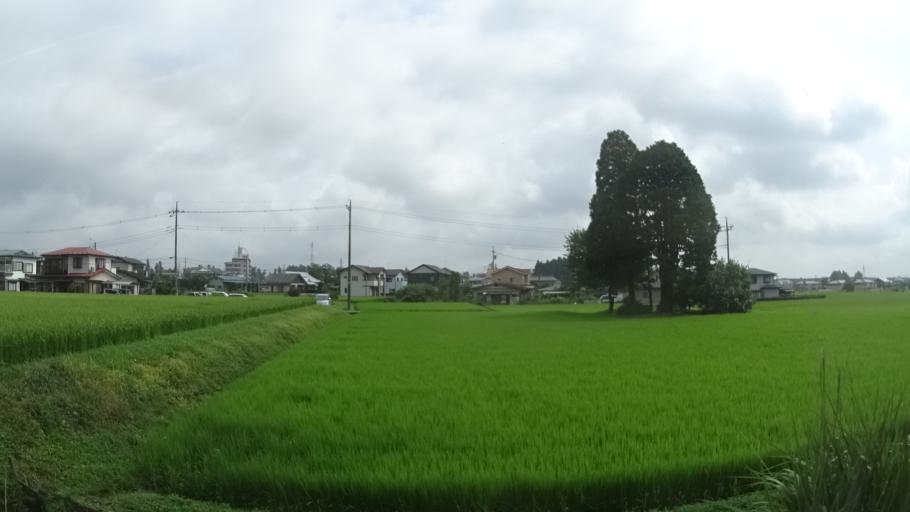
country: JP
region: Tochigi
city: Imaichi
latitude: 36.7137
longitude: 139.6978
